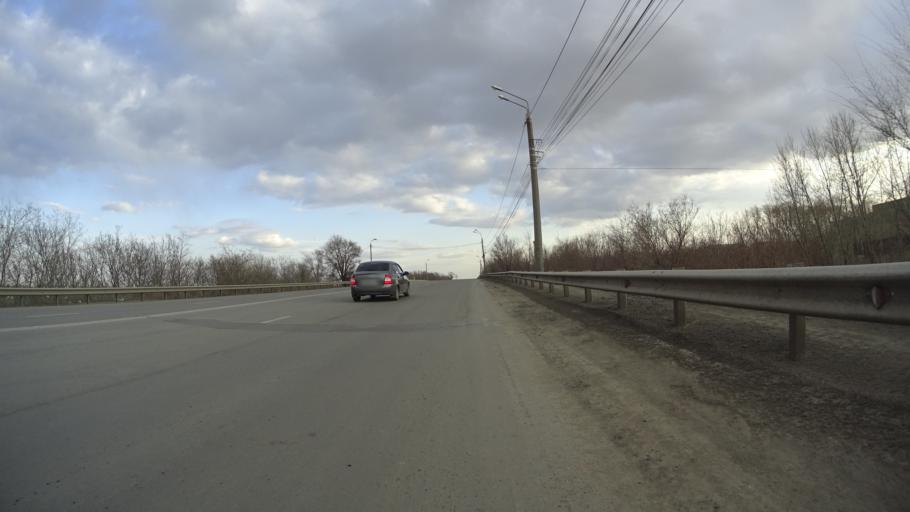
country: RU
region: Chelyabinsk
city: Novosineglazovskiy
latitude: 55.1031
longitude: 61.3874
